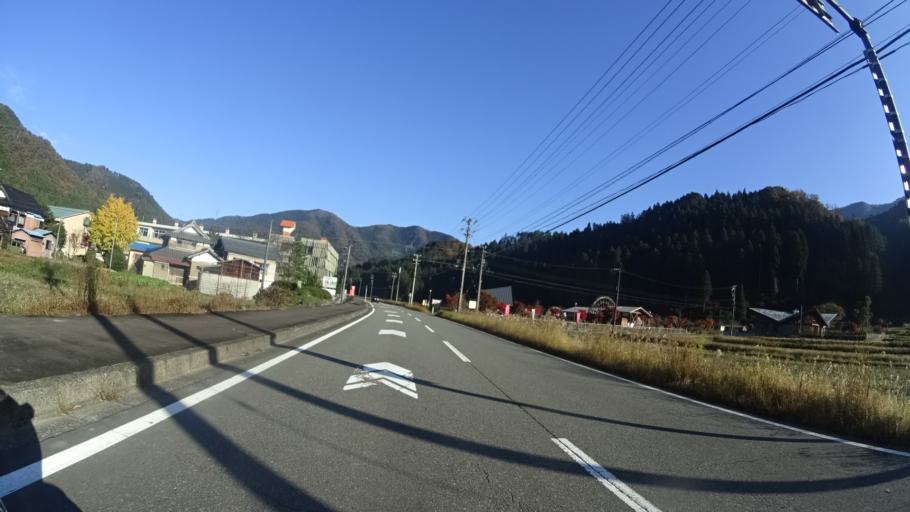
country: JP
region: Fukui
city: Maruoka
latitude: 36.1610
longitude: 136.3328
